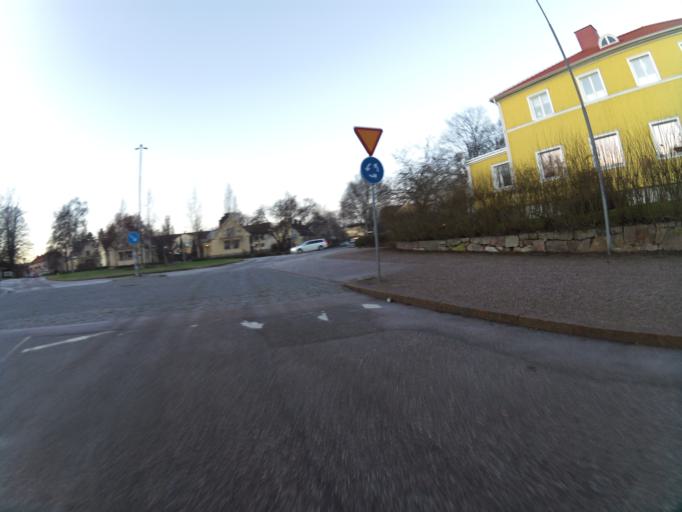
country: SE
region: Gaevleborg
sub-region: Gavle Kommun
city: Gavle
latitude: 60.6694
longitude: 17.1283
